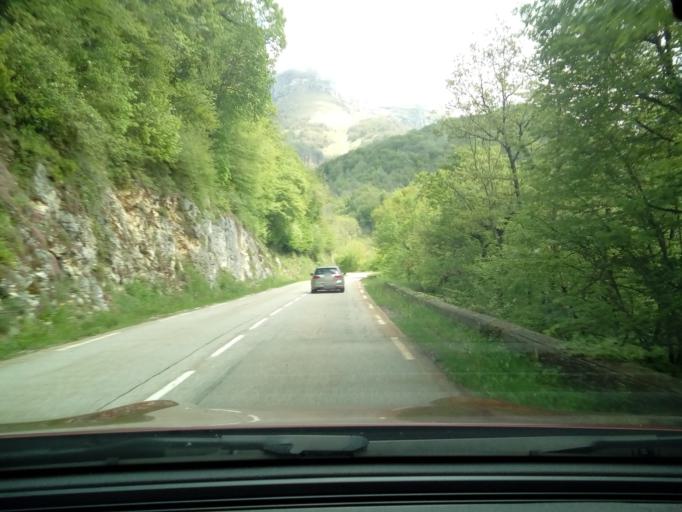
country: FR
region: Rhone-Alpes
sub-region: Departement de la Savoie
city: Barby
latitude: 45.6130
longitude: 6.0133
